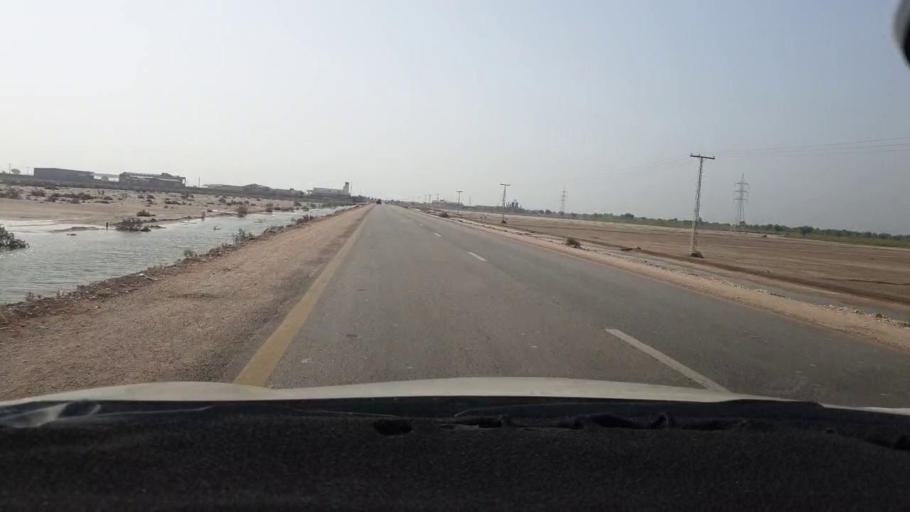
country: PK
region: Sindh
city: Sanghar
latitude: 25.9811
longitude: 68.9683
